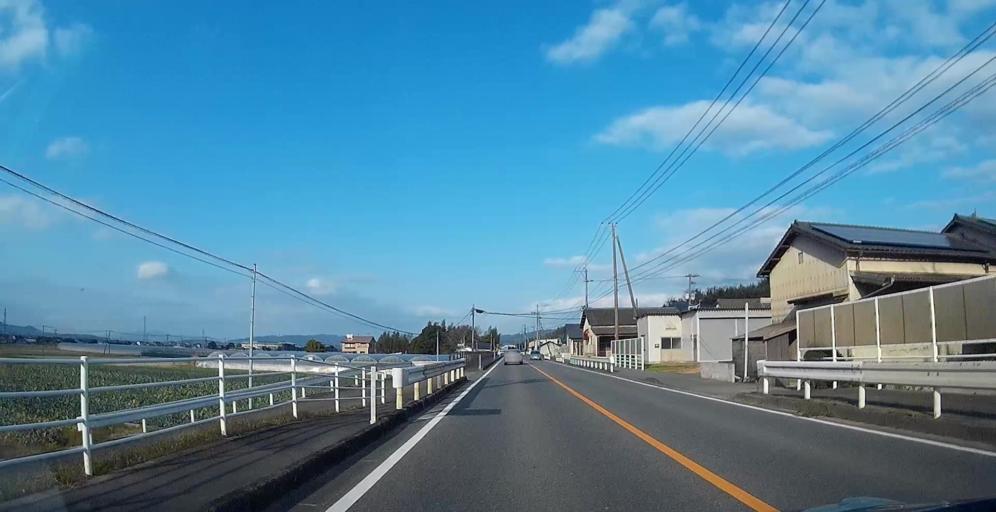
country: JP
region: Kumamoto
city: Matsubase
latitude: 32.5681
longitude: 130.6899
